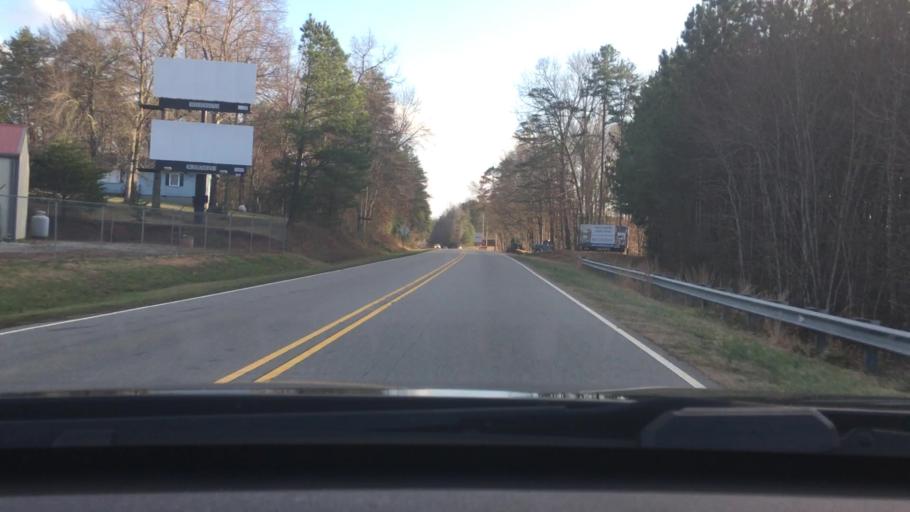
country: US
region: North Carolina
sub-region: Rutherford County
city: Rutherfordton
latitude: 35.4339
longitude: -81.9823
